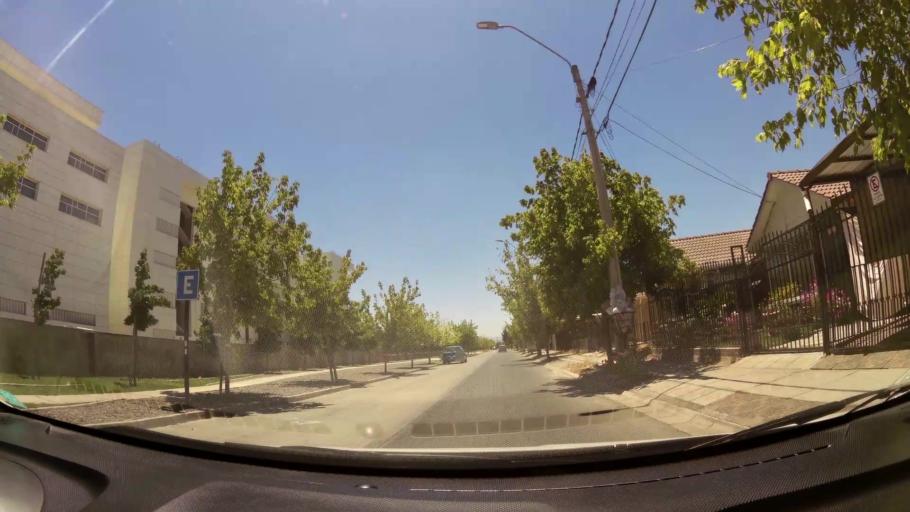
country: CL
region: O'Higgins
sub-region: Provincia de Cachapoal
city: Rancagua
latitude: -34.1554
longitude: -70.7657
